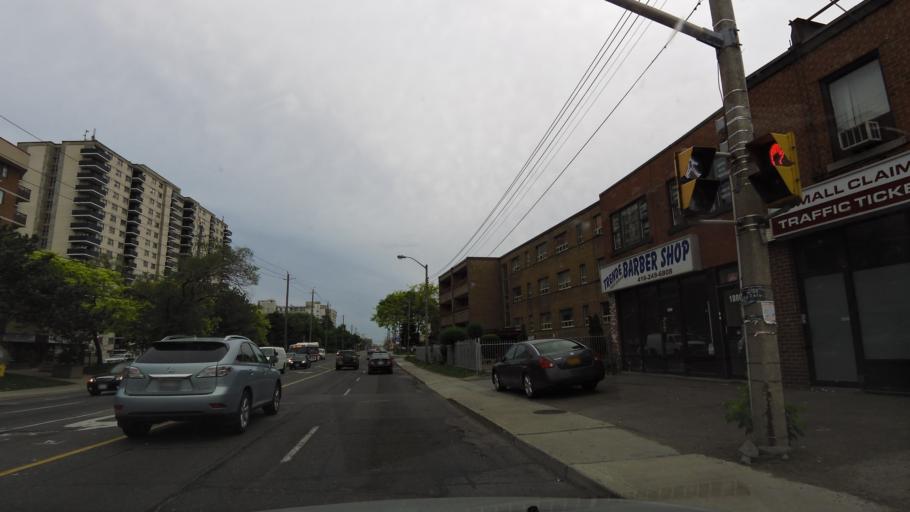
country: CA
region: Ontario
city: Etobicoke
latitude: 43.7092
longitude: -79.5056
